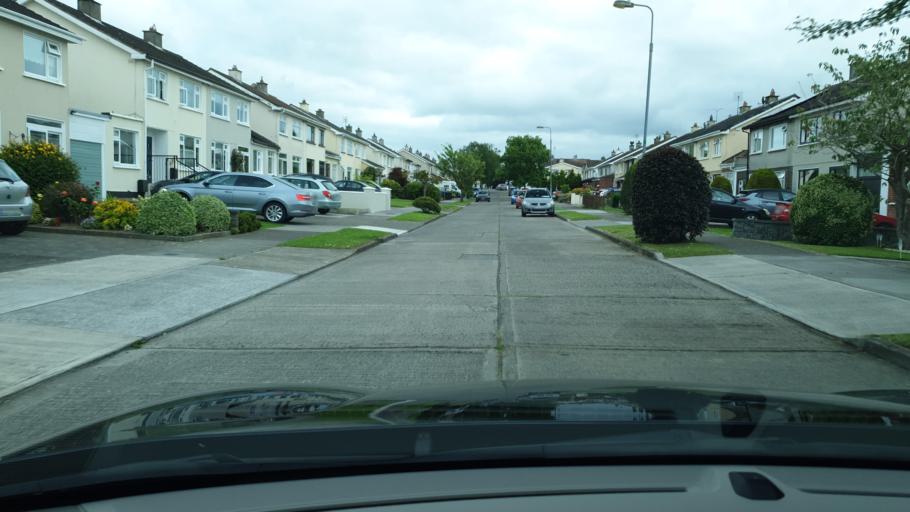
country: IE
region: Leinster
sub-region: An Mhi
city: Ashbourne
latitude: 53.5065
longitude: -6.4034
